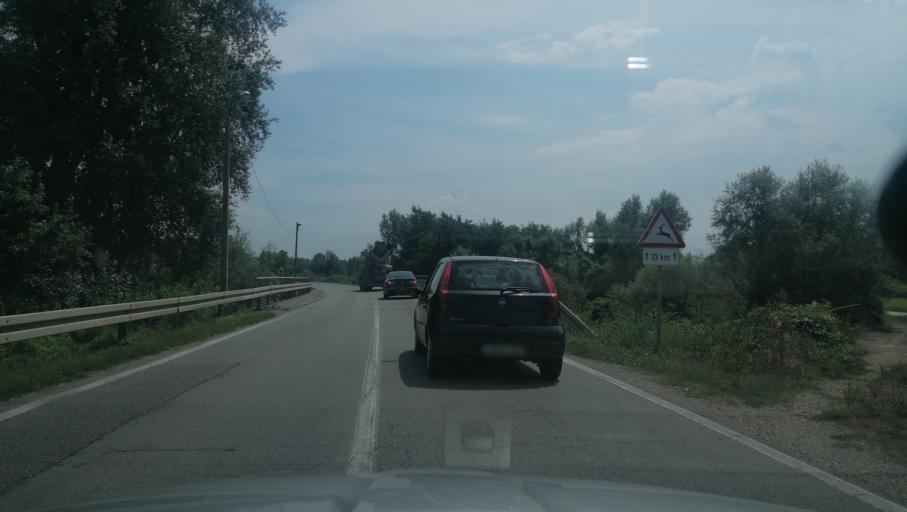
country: BA
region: Republika Srpska
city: Velika Obarska
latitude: 44.8287
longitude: 19.0297
